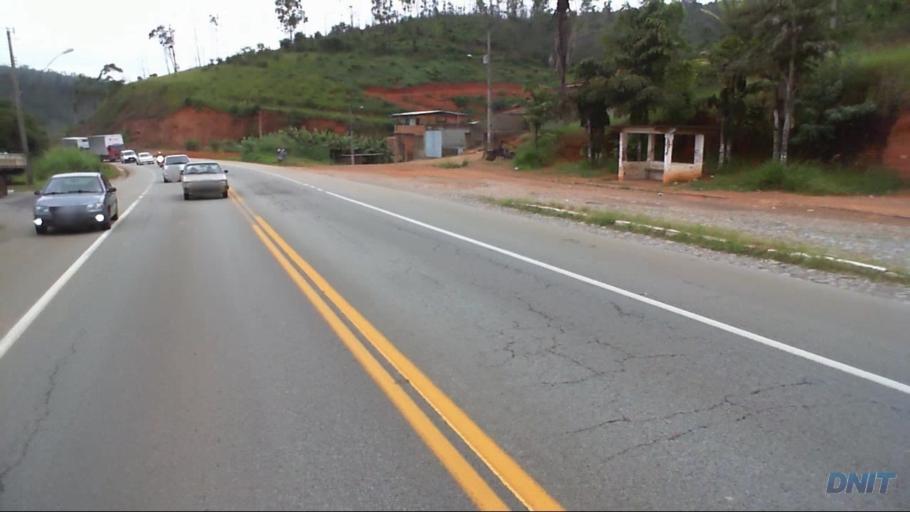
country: BR
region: Minas Gerais
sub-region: Joao Monlevade
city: Joao Monlevade
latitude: -19.8281
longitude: -43.0873
